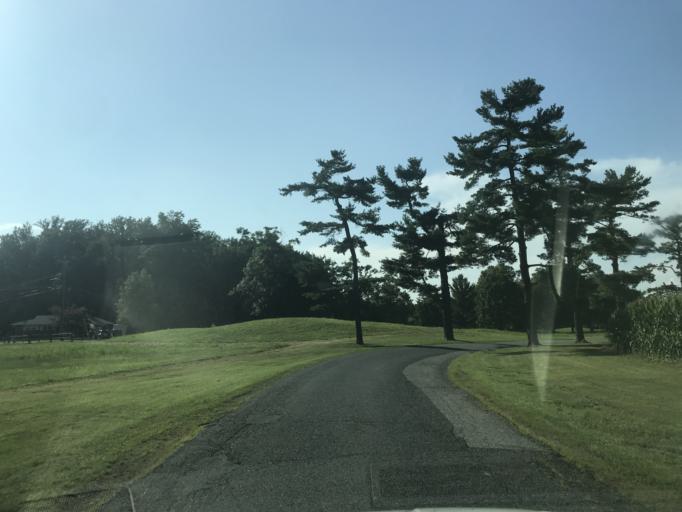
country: US
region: Maryland
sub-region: Harford County
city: Aberdeen
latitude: 39.5076
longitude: -76.1264
